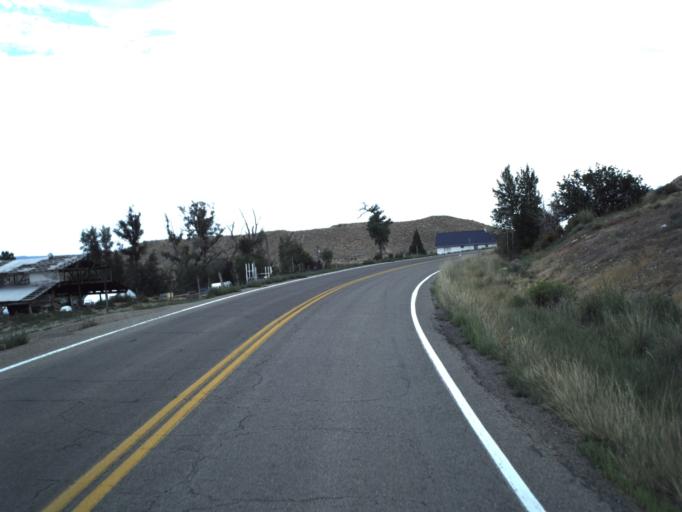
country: US
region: Utah
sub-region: Emery County
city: Huntington
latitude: 39.3694
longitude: -110.8507
